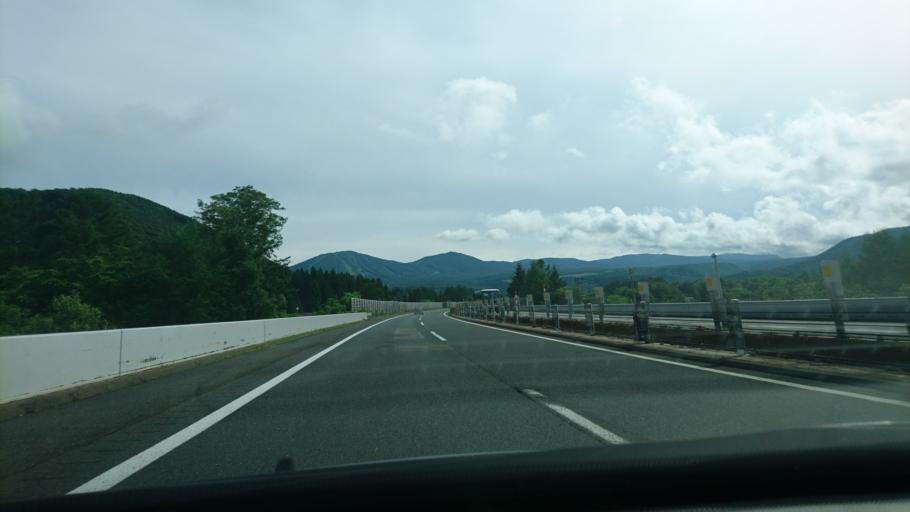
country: JP
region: Akita
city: Hanawa
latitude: 40.0365
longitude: 140.9897
